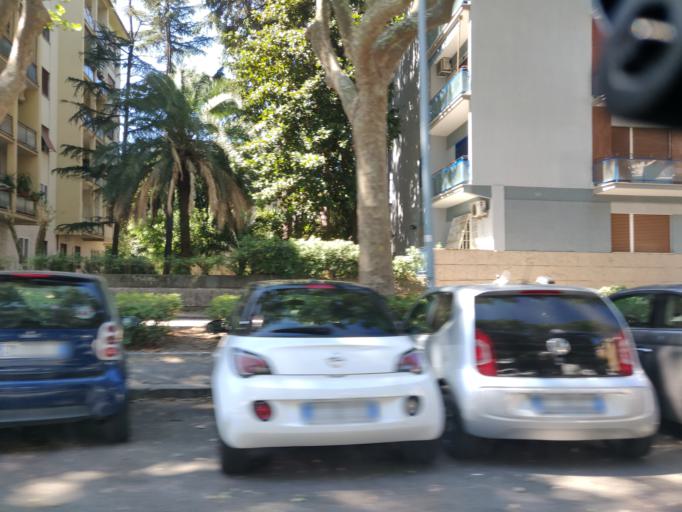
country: IT
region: Latium
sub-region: Citta metropolitana di Roma Capitale
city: Selcetta
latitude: 41.8262
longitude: 12.4748
